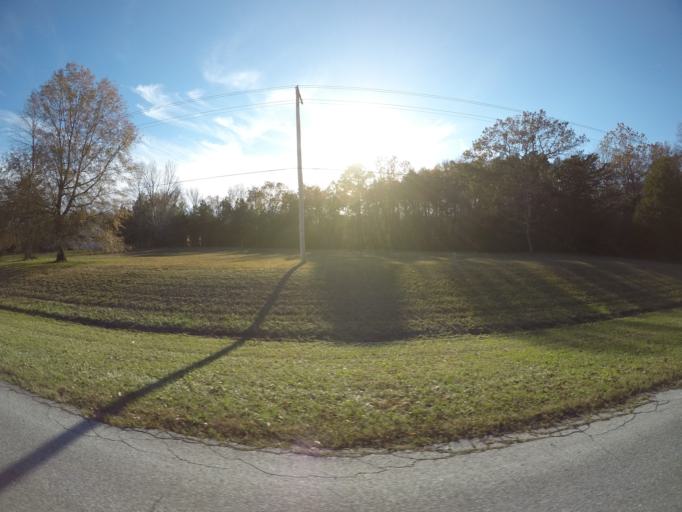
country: US
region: Maryland
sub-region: Saint Mary's County
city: Leonardtown
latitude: 38.3201
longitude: -76.6715
